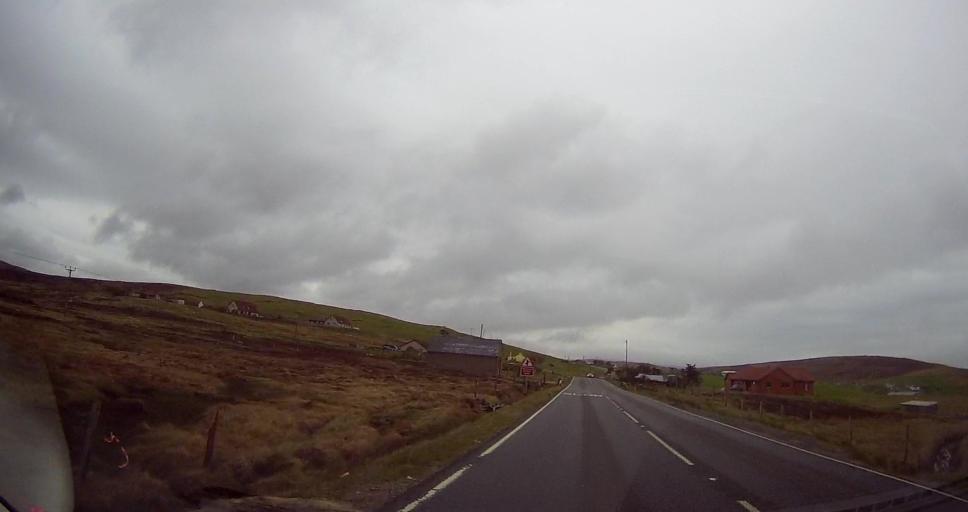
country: GB
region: Scotland
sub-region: Shetland Islands
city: Lerwick
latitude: 60.2336
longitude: -1.2344
